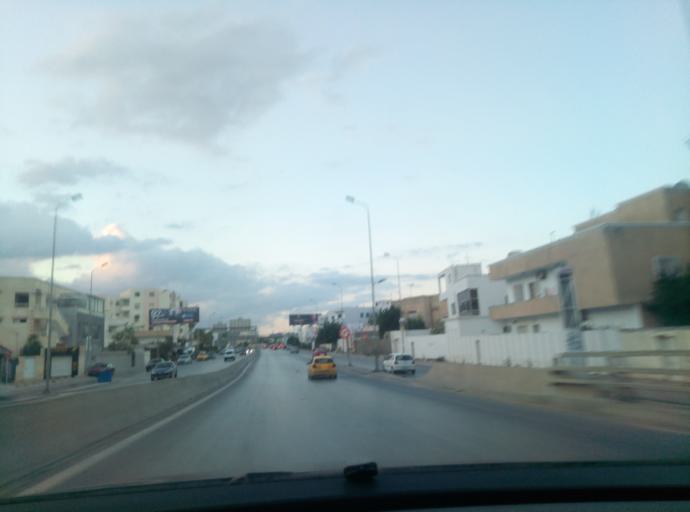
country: TN
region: Manouba
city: Manouba
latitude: 36.8045
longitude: 10.1186
